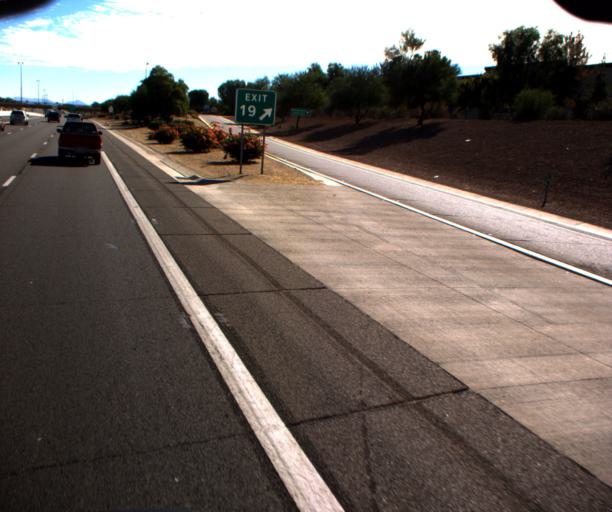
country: US
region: Arizona
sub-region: Maricopa County
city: Peoria
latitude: 33.6681
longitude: -112.1915
